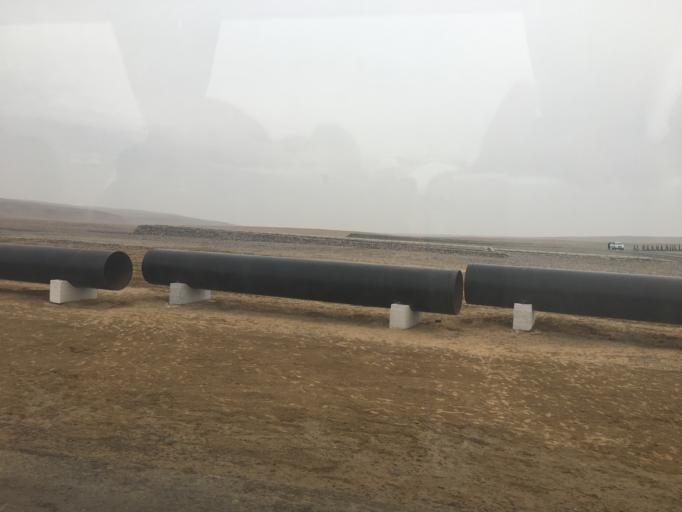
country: TM
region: Mary
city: Serhetabat
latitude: 35.3832
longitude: 62.1790
